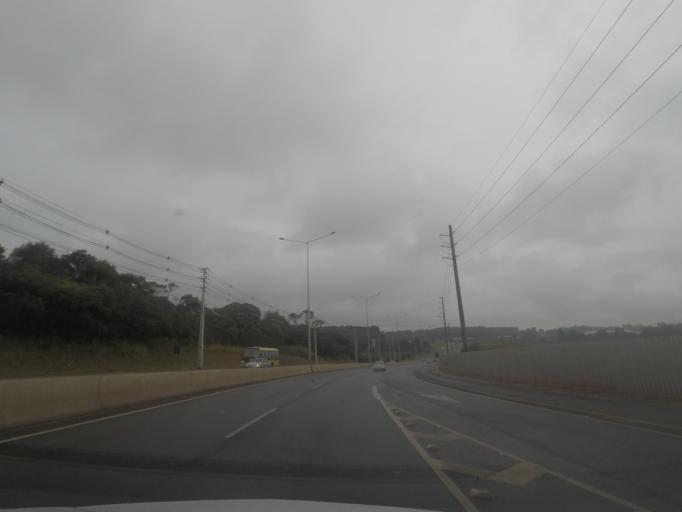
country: BR
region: Parana
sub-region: Piraquara
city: Piraquara
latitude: -25.4592
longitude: -49.0807
